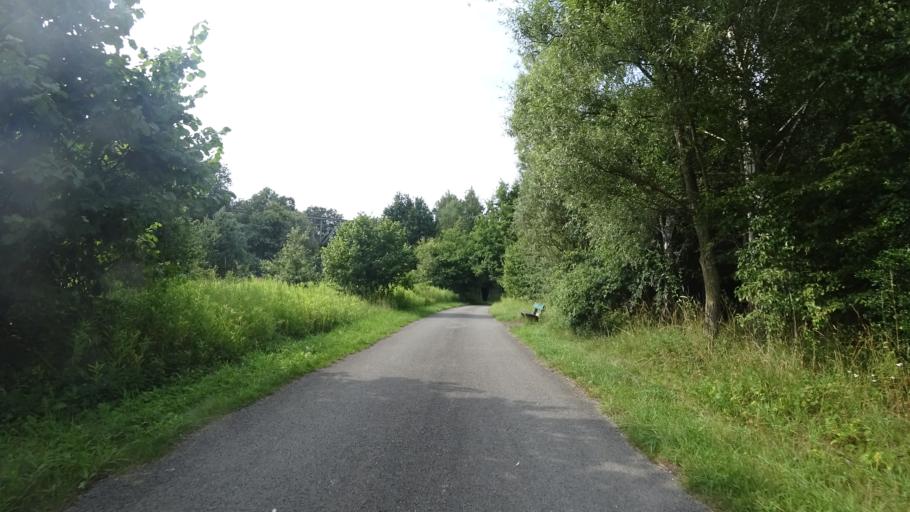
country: DE
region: North Rhine-Westphalia
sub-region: Regierungsbezirk Detmold
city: Guetersloh
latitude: 51.9330
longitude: 8.4291
